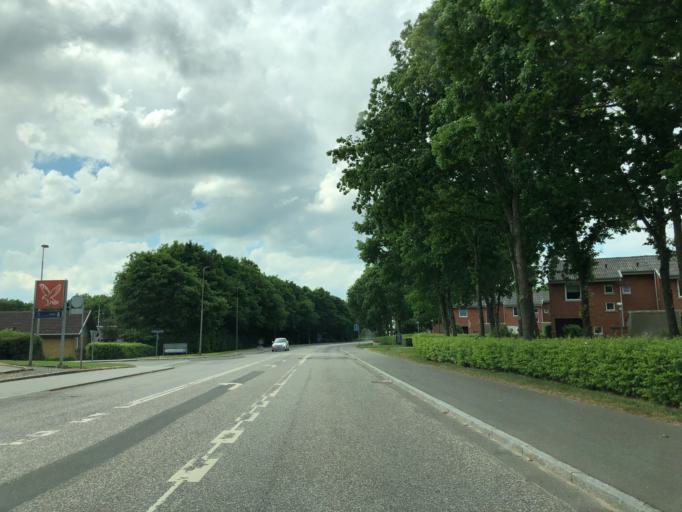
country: DK
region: Central Jutland
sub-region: Struer Kommune
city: Struer
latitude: 56.4819
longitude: 8.5896
